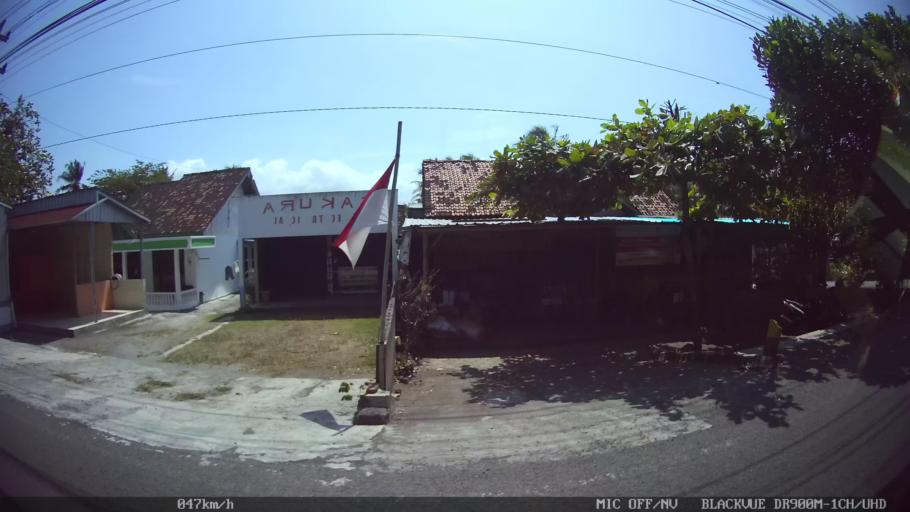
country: ID
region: Daerah Istimewa Yogyakarta
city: Srandakan
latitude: -7.9097
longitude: 110.0859
